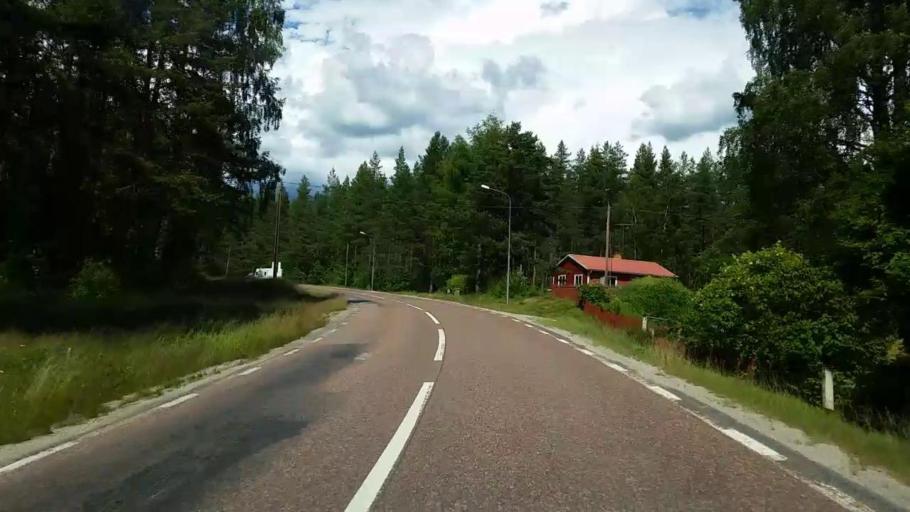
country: SE
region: Gaevleborg
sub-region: Ovanakers Kommun
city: Edsbyn
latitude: 61.3052
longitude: 15.5104
